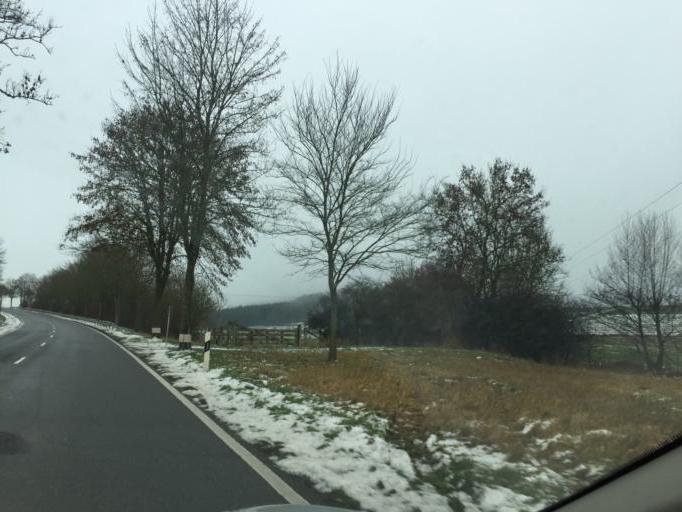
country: LU
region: Diekirch
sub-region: Canton de Diekirch
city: Mertzig
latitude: 49.8297
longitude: 5.9921
